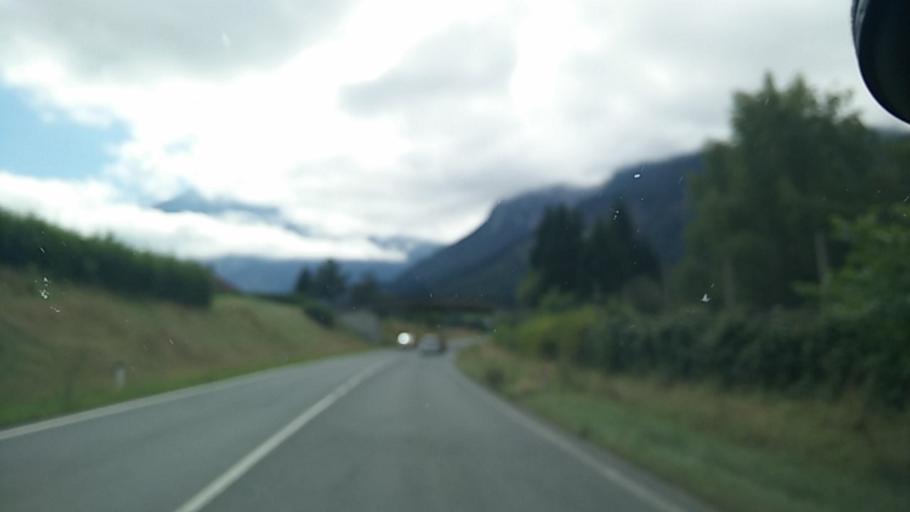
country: AT
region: Carinthia
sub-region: Politischer Bezirk Klagenfurt Land
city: Maria Rain
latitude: 46.5352
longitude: 14.2665
